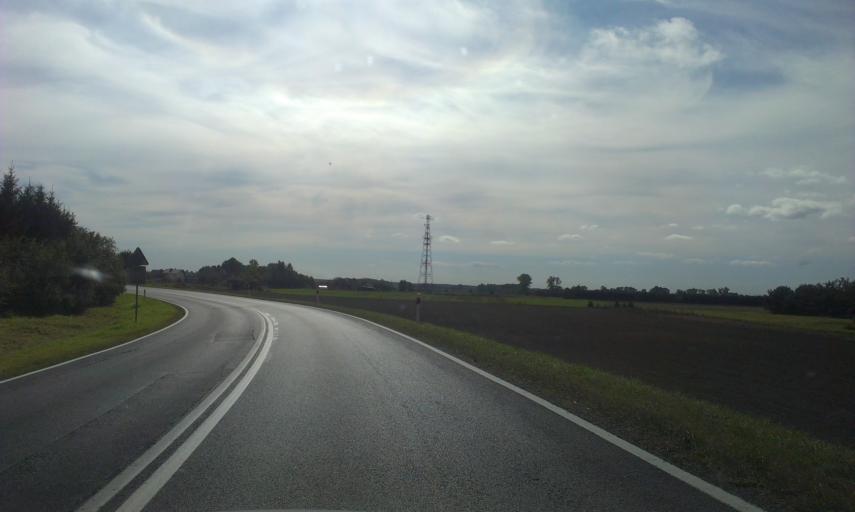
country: PL
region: Greater Poland Voivodeship
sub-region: Powiat zlotowski
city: Okonek
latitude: 53.6054
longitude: 16.7978
